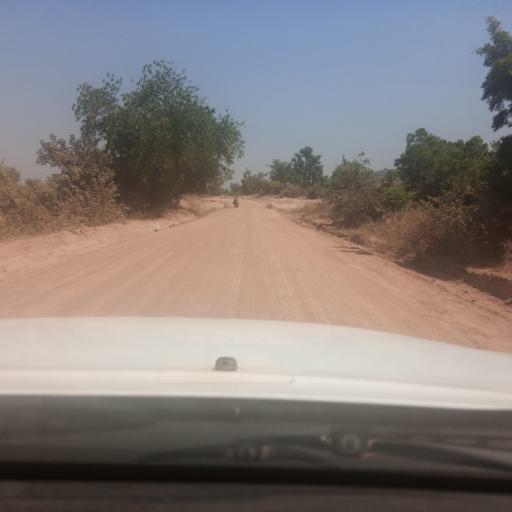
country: NG
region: Adamawa
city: Yola
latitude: 9.0934
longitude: 12.3894
